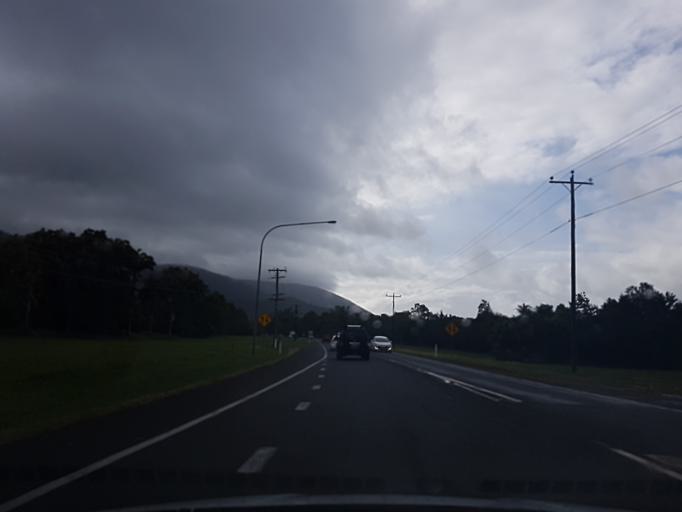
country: AU
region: Queensland
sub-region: Cairns
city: Trinity Beach
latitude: -16.7906
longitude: 145.6776
